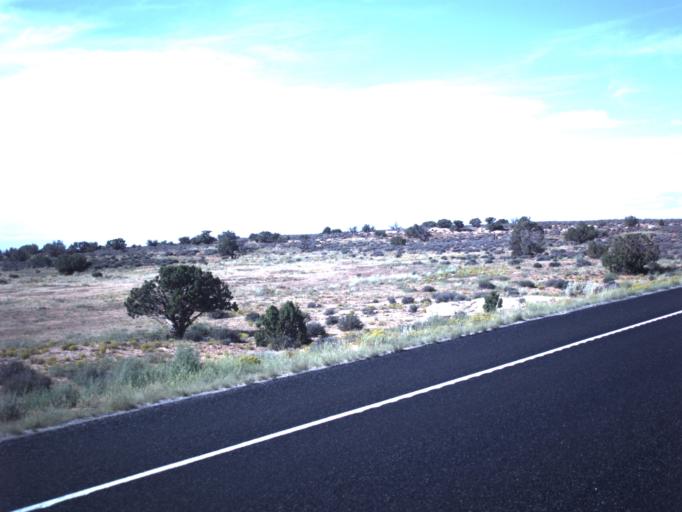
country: US
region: Utah
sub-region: Grand County
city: Moab
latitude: 38.6184
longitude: -109.8132
